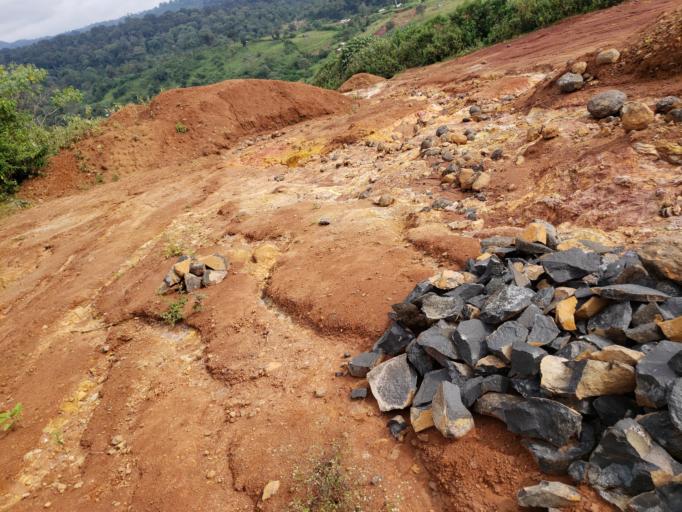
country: ET
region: Oromiya
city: Dodola
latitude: 6.5444
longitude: 39.4223
